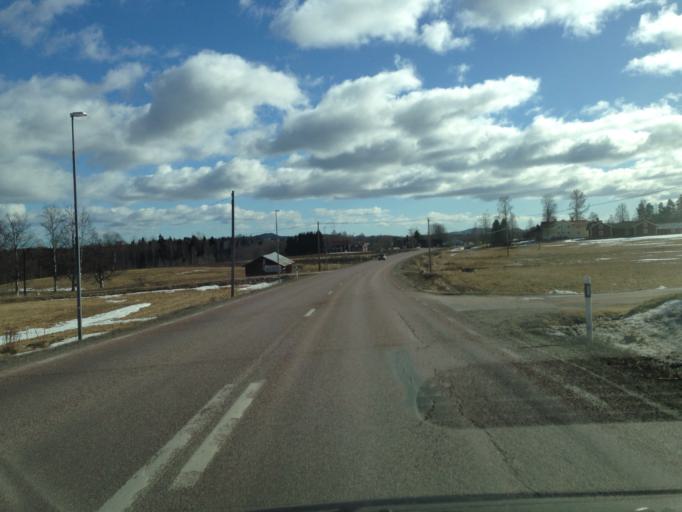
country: SE
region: Gaevleborg
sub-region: Ljusdals Kommun
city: Farila
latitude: 61.7998
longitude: 15.8091
